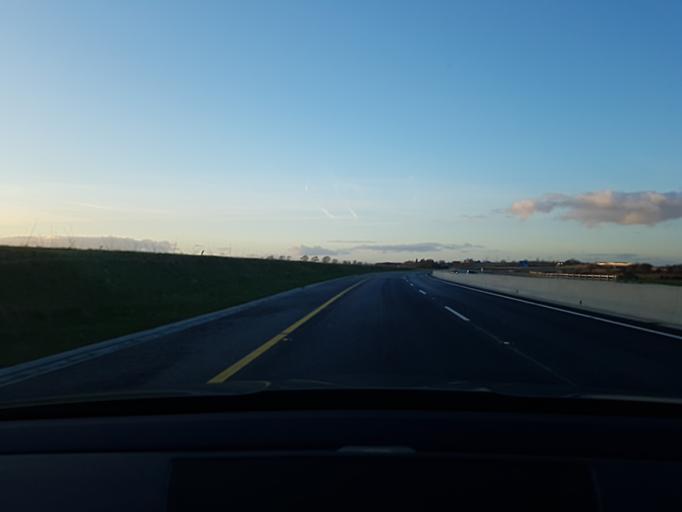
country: IE
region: Connaught
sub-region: County Galway
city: Tuam
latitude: 53.4927
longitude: -8.8729
